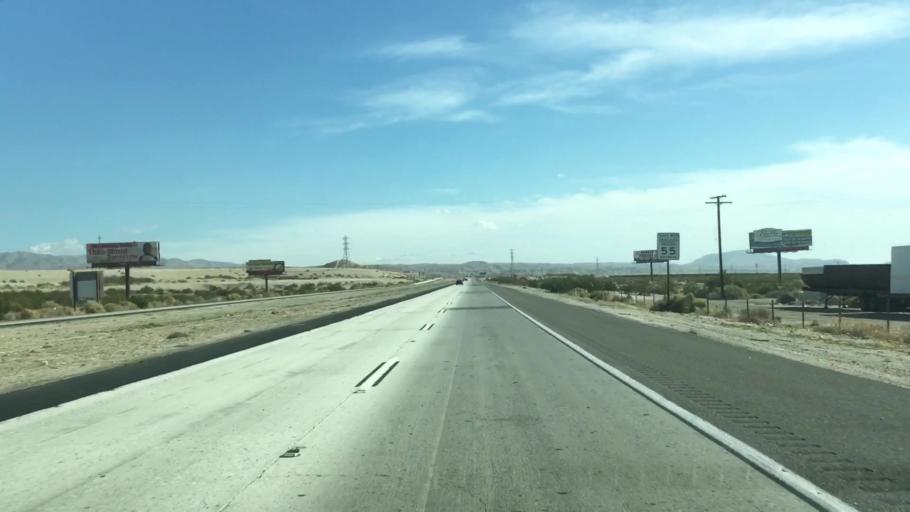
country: US
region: California
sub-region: Riverside County
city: Coachella
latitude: 33.7114
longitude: -116.1561
